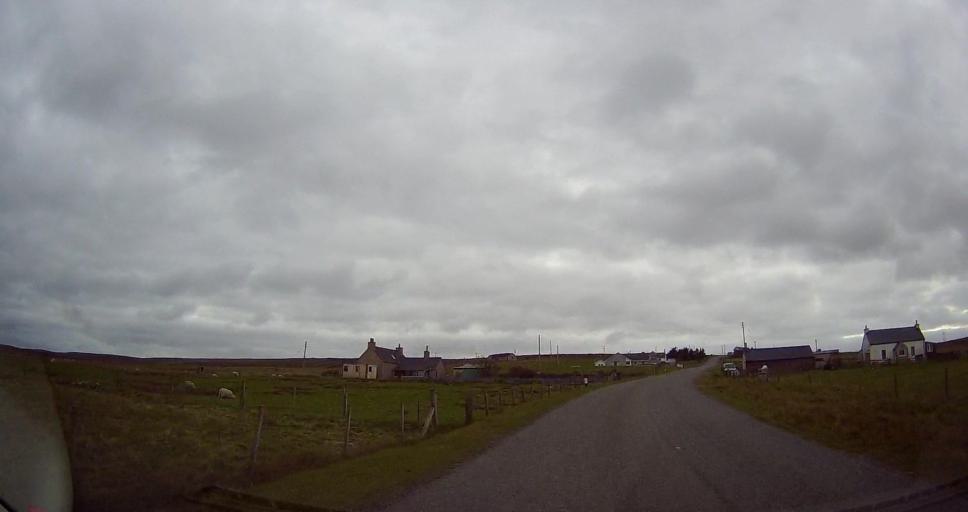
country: GB
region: Scotland
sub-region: Shetland Islands
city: Shetland
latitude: 60.6711
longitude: -0.9997
